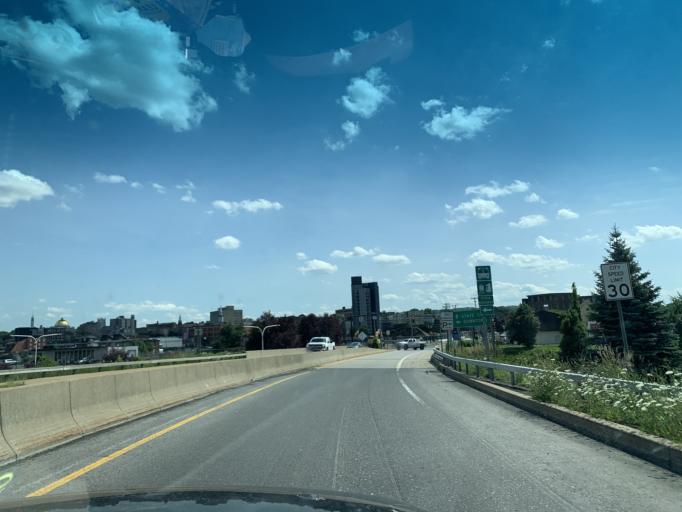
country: US
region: New York
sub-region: Oneida County
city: Utica
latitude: 43.1061
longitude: -75.2372
